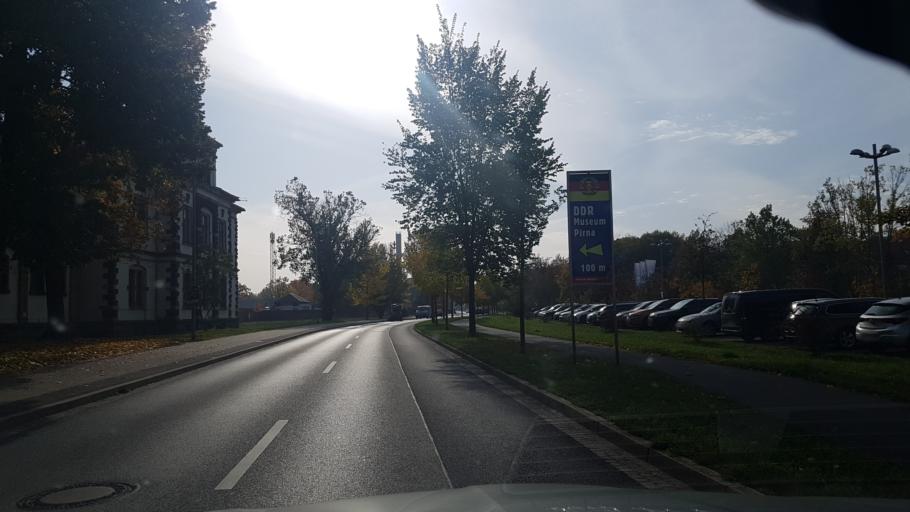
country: DE
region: Saxony
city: Pirna
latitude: 50.9458
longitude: 13.9430
